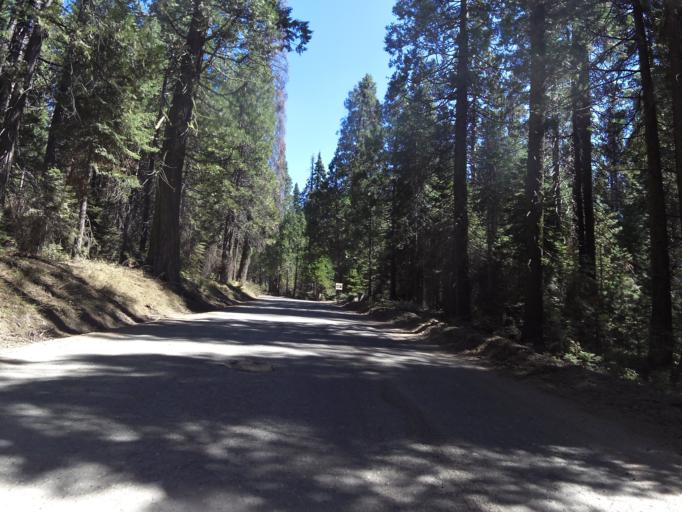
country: US
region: California
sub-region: Madera County
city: Oakhurst
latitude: 37.4124
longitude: -119.5692
